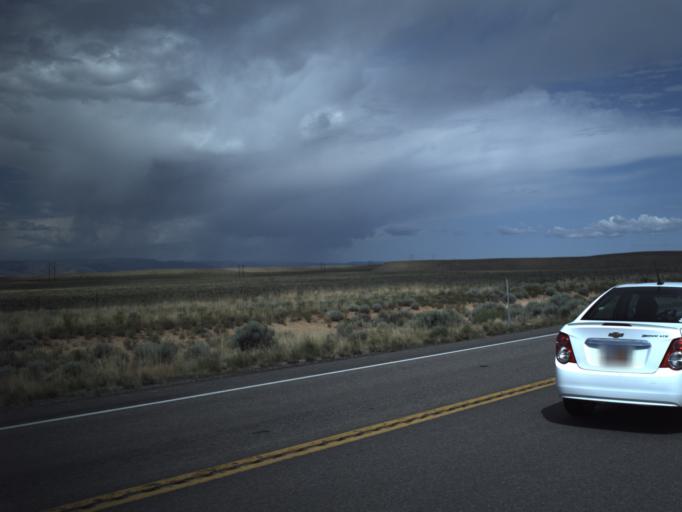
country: US
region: Utah
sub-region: Carbon County
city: East Carbon City
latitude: 39.4908
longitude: -110.5188
